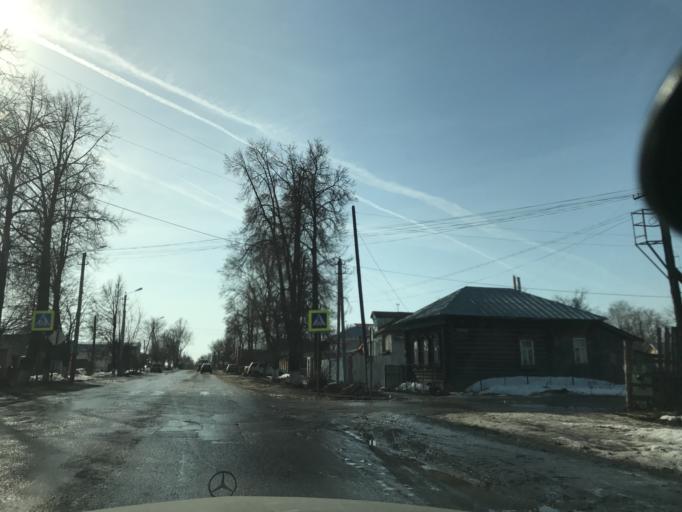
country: RU
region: Nizjnij Novgorod
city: Taremskoye
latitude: 55.9576
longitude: 43.0481
